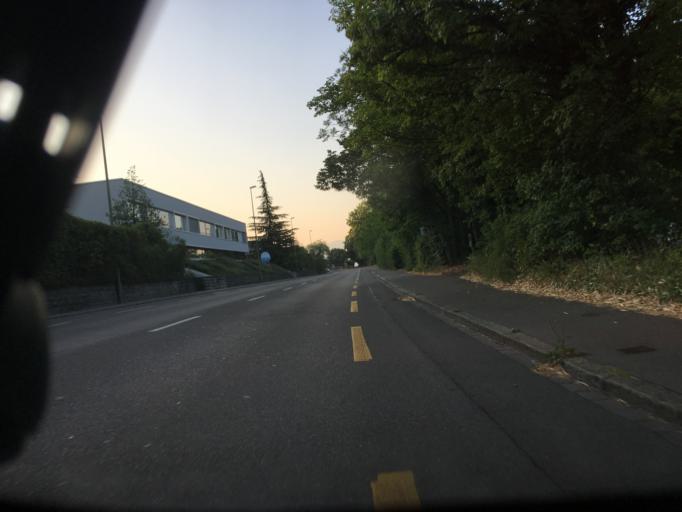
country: CH
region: Zurich
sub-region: Bezirk Meilen
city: Feldmeilen
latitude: 47.2729
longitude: 8.6269
